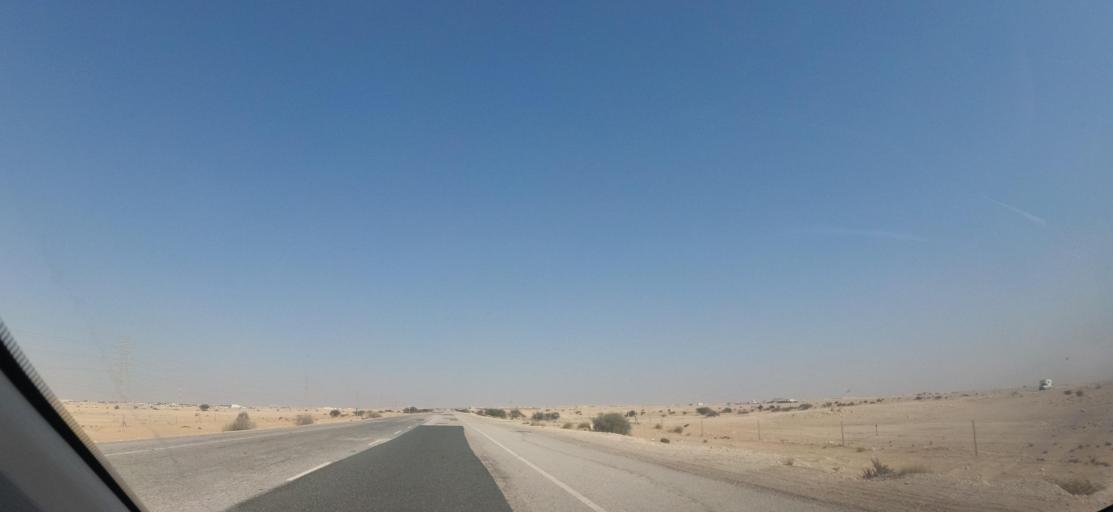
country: QA
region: Baladiyat ar Rayyan
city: Dukhan
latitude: 25.4784
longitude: 50.9529
